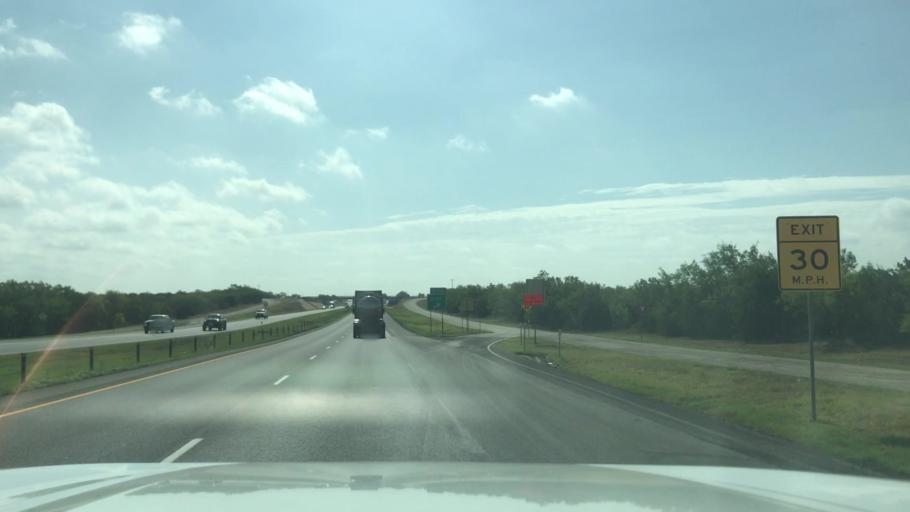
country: US
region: Texas
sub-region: Nolan County
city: Sweetwater
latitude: 32.4900
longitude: -100.2219
